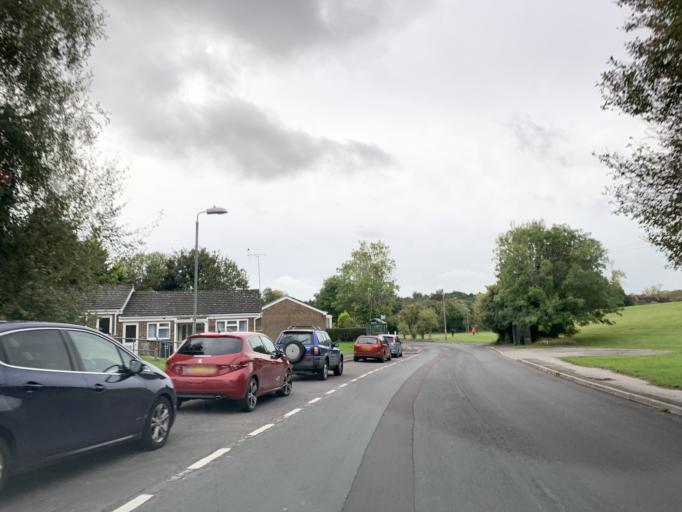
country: GB
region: England
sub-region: Wiltshire
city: Bishopstrow
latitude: 51.1985
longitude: -2.1566
